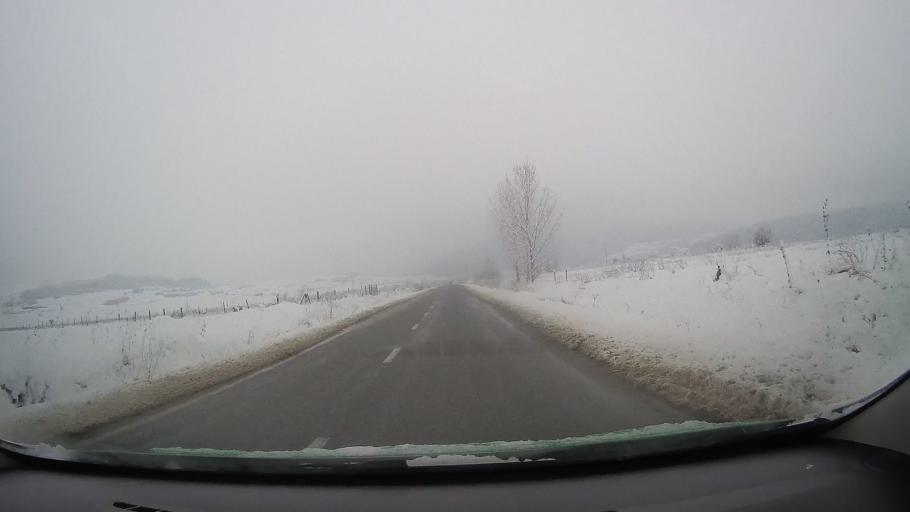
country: RO
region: Sibiu
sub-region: Comuna Orlat
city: Orlat
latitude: 45.7783
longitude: 23.9452
